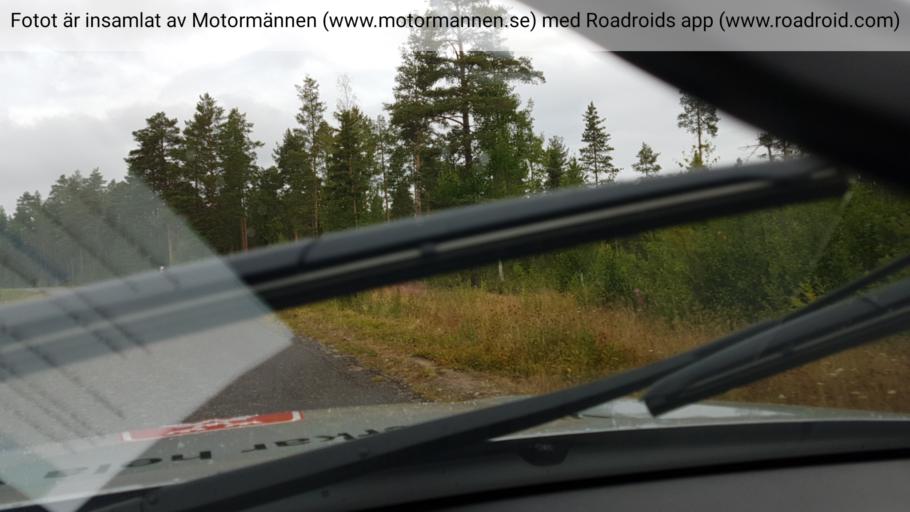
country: SE
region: Norrbotten
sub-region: Alvsbyns Kommun
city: AElvsbyn
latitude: 66.0759
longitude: 20.9213
